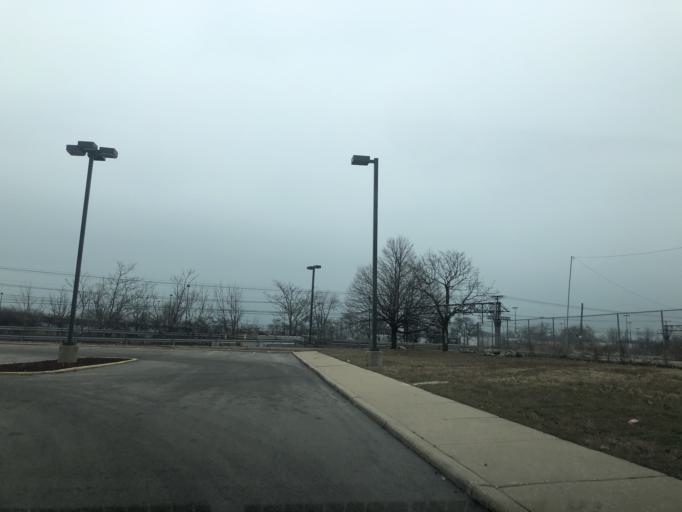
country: US
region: Illinois
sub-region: Cook County
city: Chicago
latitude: 41.8459
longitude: -87.6153
